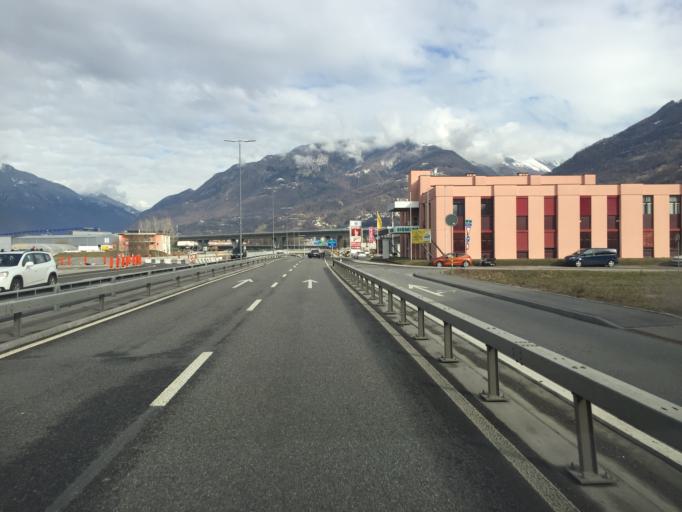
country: CH
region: Ticino
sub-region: Bellinzona District
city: Camorino
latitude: 46.1594
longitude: 8.9813
